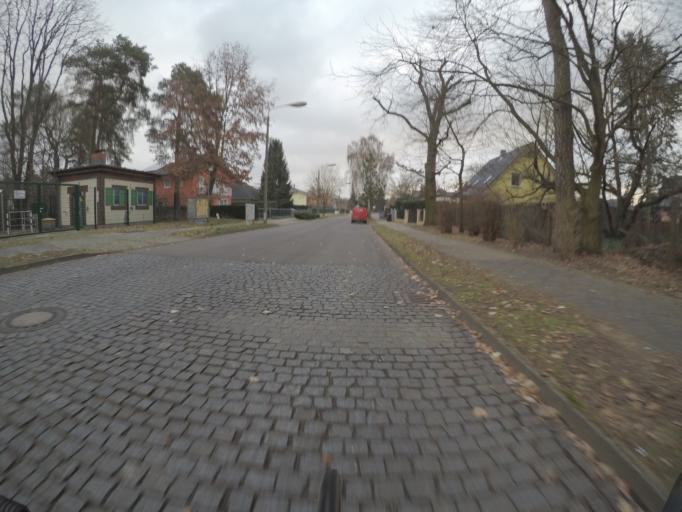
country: DE
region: Berlin
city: Kopenick Bezirk
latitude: 52.4664
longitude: 13.5687
